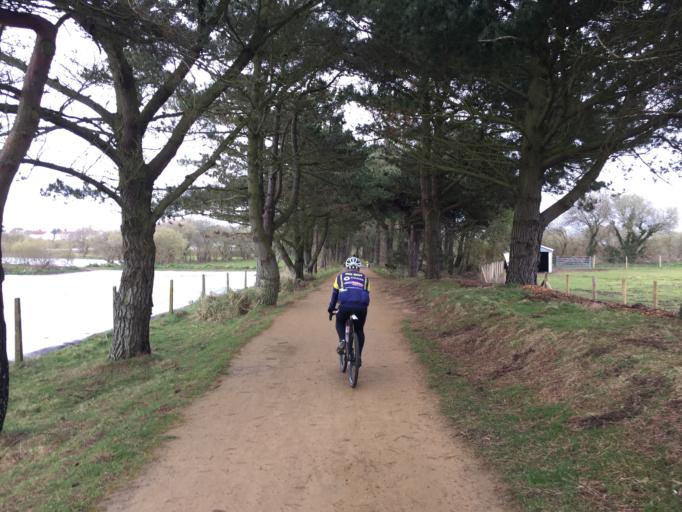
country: JE
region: St Helier
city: Saint Helier
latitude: 49.1813
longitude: -2.2285
